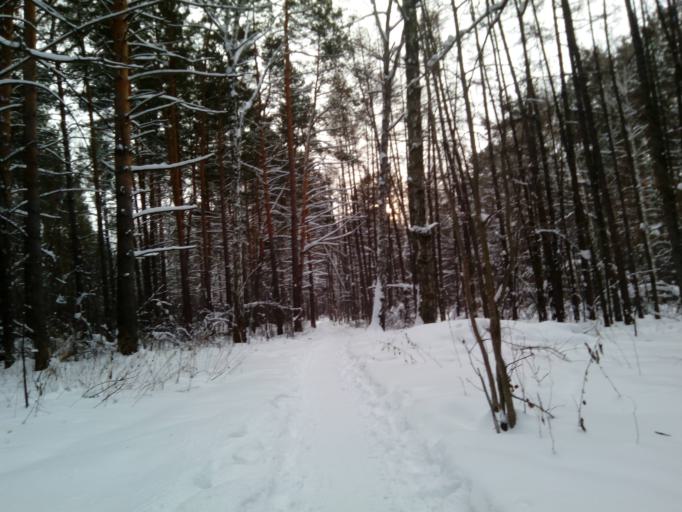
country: RU
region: Novosibirsk
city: Akademgorodok
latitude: 54.8575
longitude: 83.0928
